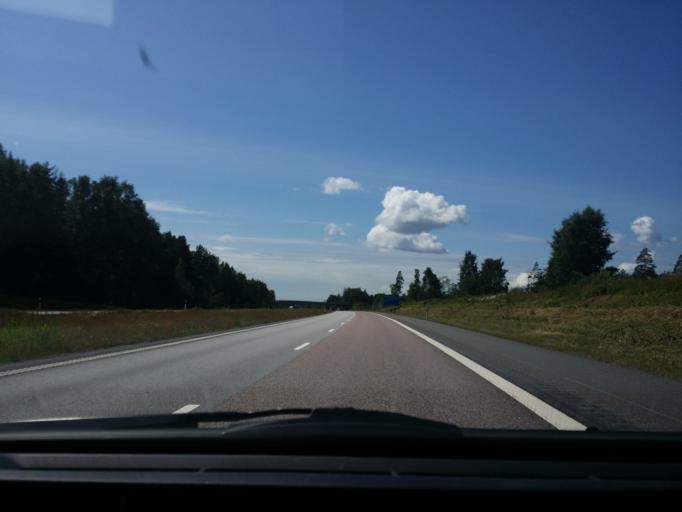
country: SE
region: OErebro
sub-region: Lindesbergs Kommun
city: Frovi
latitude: 59.3153
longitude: 15.4391
